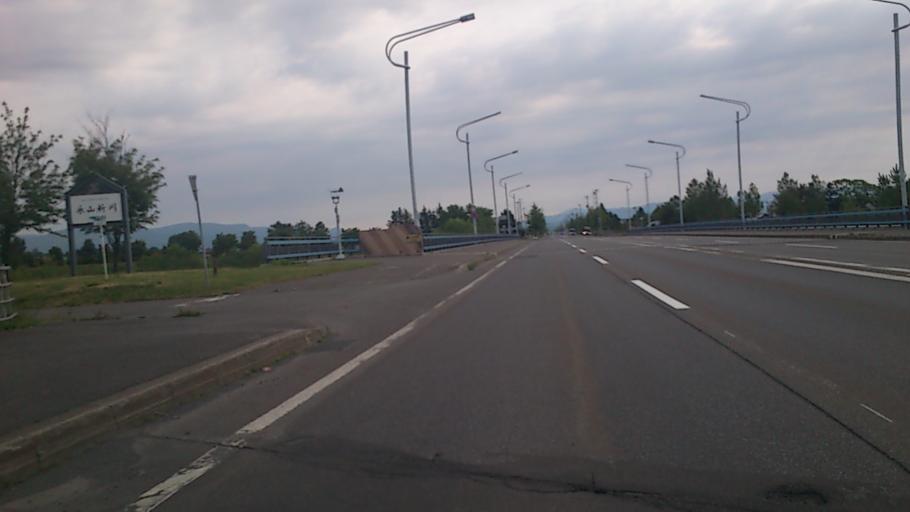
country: JP
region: Hokkaido
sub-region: Asahikawa-shi
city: Asahikawa
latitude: 43.8208
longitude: 142.4501
